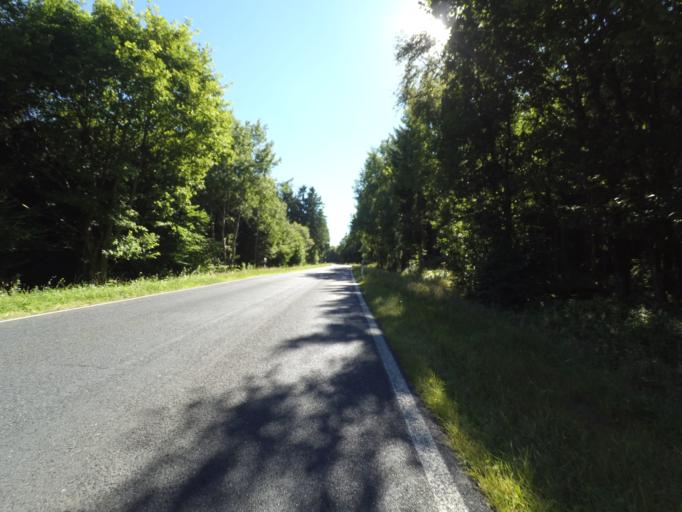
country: DE
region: Rheinland-Pfalz
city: Dreis-Bruck
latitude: 50.2882
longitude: 6.8073
